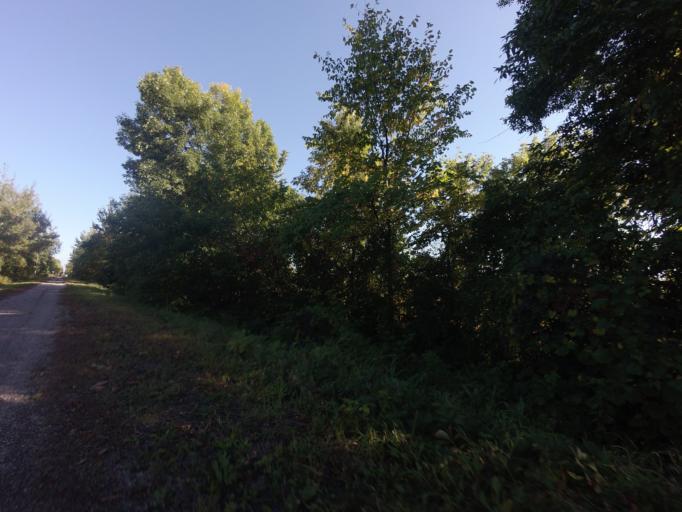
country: CA
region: Ontario
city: Hawkesbury
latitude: 45.5211
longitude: -74.5343
